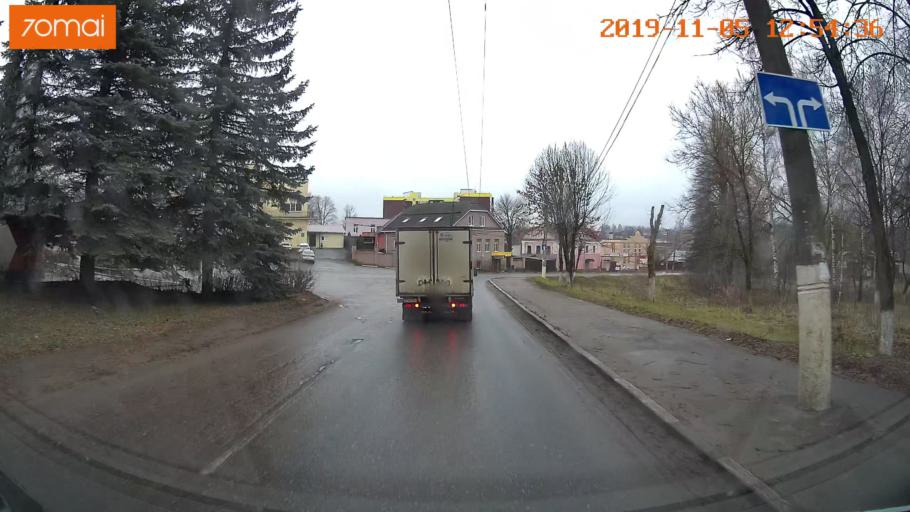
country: RU
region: Ivanovo
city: Kokhma
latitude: 56.9313
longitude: 41.0931
